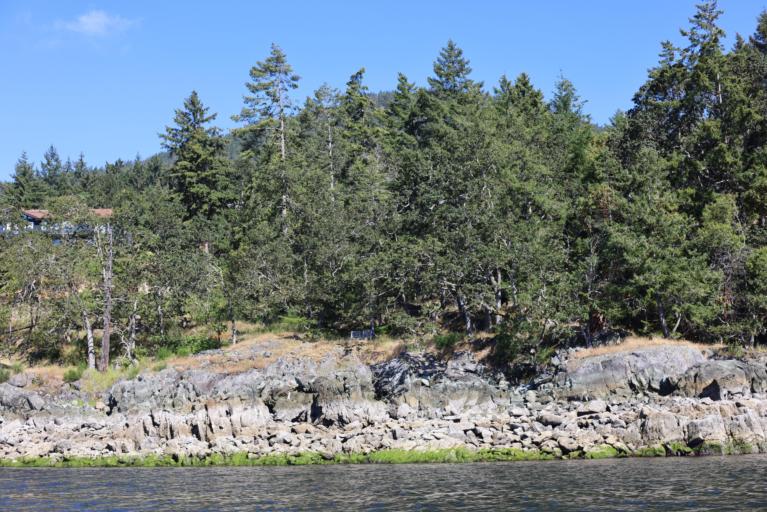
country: CA
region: British Columbia
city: North Cowichan
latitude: 48.8213
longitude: -123.5864
